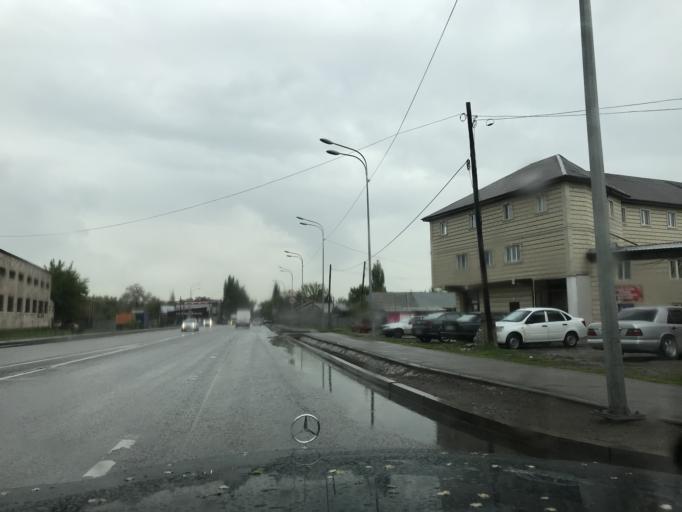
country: KZ
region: Almaty Oblysy
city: Pervomayskiy
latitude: 43.3402
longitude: 76.9661
